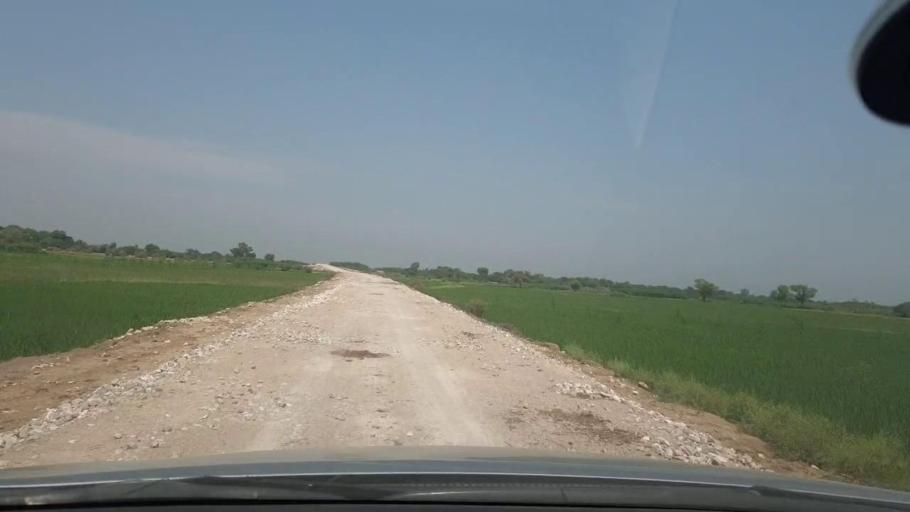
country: PK
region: Balochistan
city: Garhi Khairo
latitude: 28.0591
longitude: 67.9994
